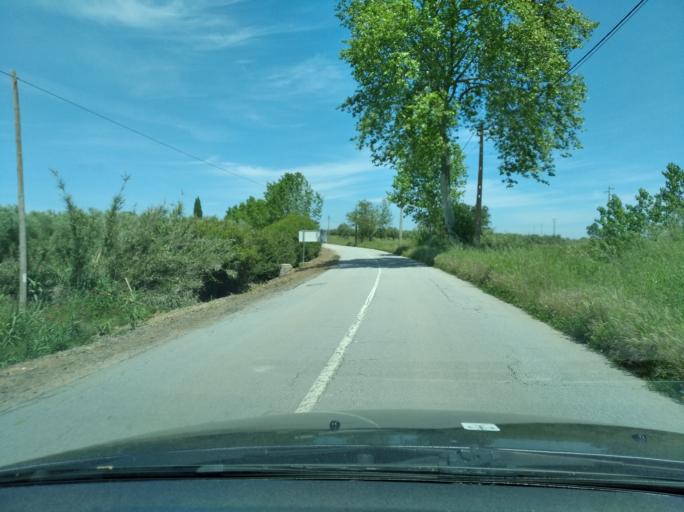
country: PT
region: Portalegre
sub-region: Avis
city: Avis
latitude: 39.0847
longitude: -7.8791
